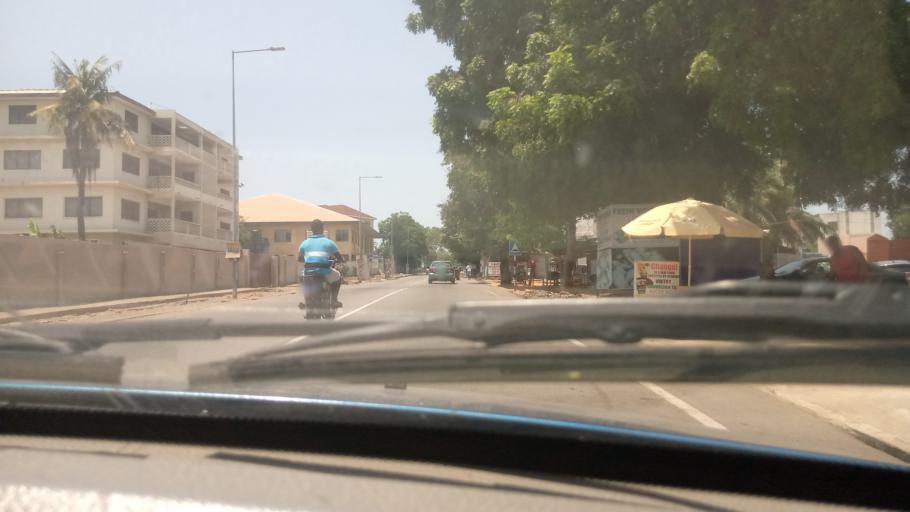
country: GH
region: Greater Accra
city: Accra
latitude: 5.5486
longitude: -0.2307
